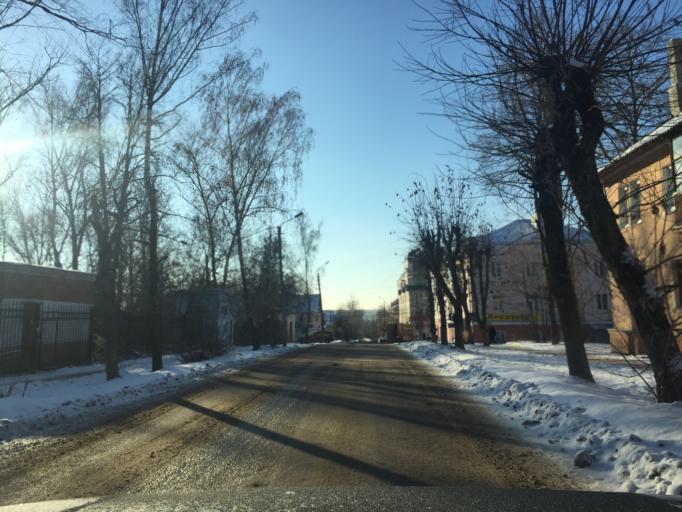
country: RU
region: Tula
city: Tula
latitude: 54.1858
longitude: 37.6989
